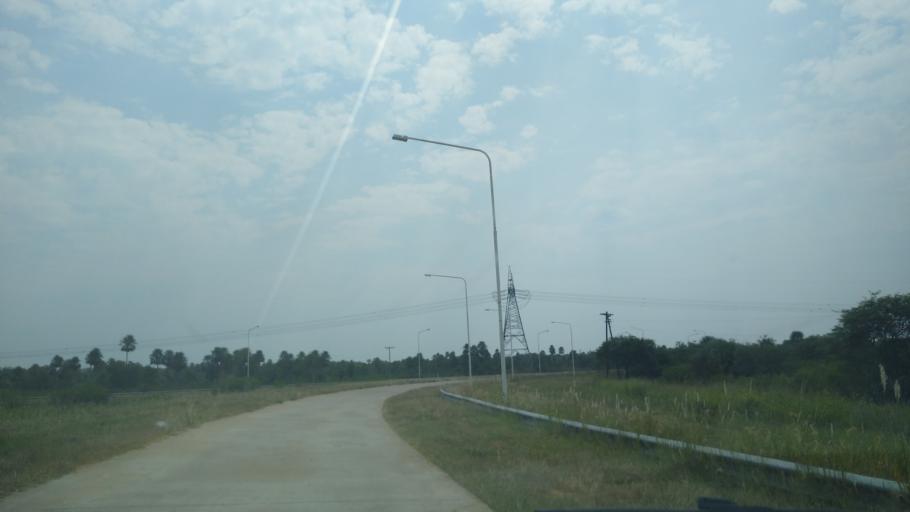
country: AR
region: Chaco
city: Margarita Belen
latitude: -27.0855
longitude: -58.9579
